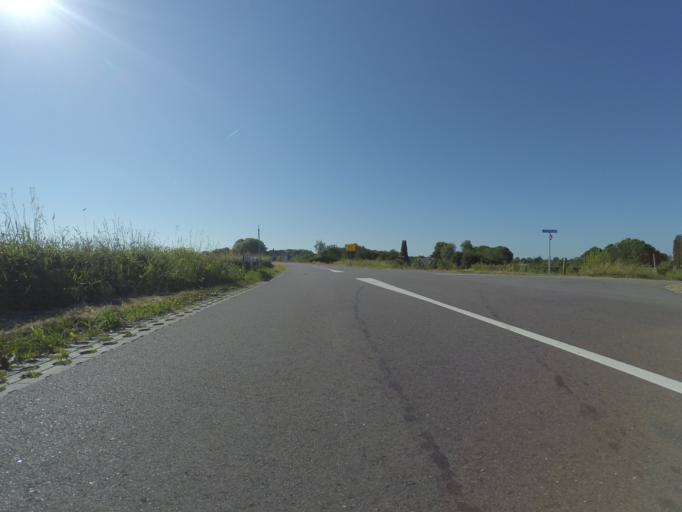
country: NL
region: Gelderland
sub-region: Gemeente Voorst
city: Twello
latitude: 52.2651
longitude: 6.1182
